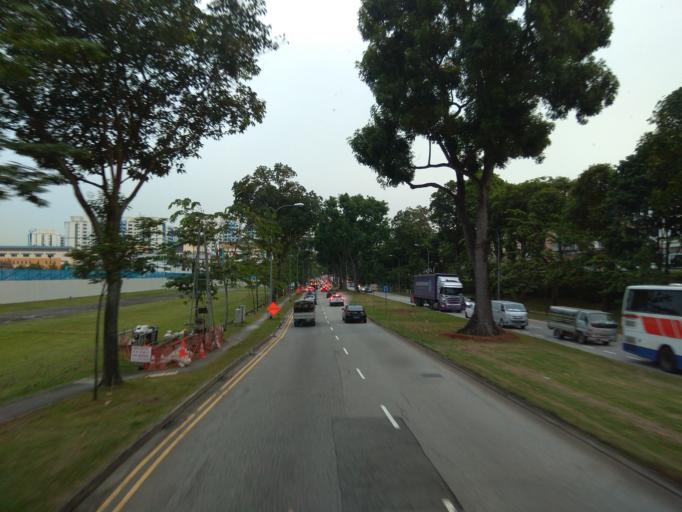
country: MY
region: Johor
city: Johor Bahru
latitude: 1.3545
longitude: 103.6987
